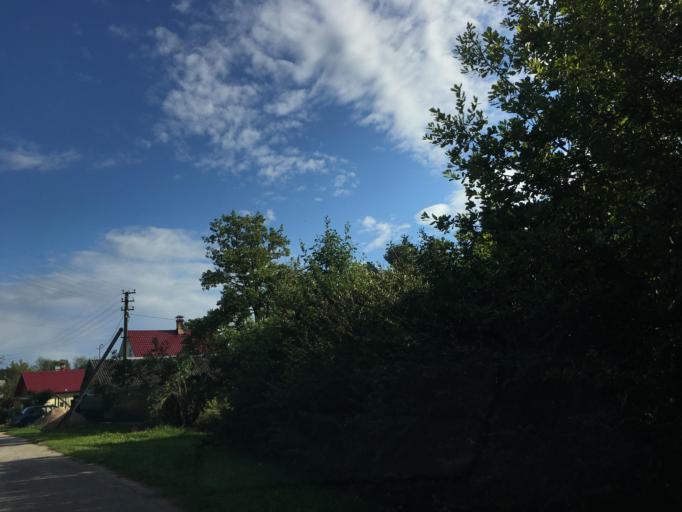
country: RU
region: Pskov
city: Izborsk
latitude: 57.7715
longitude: 27.9724
